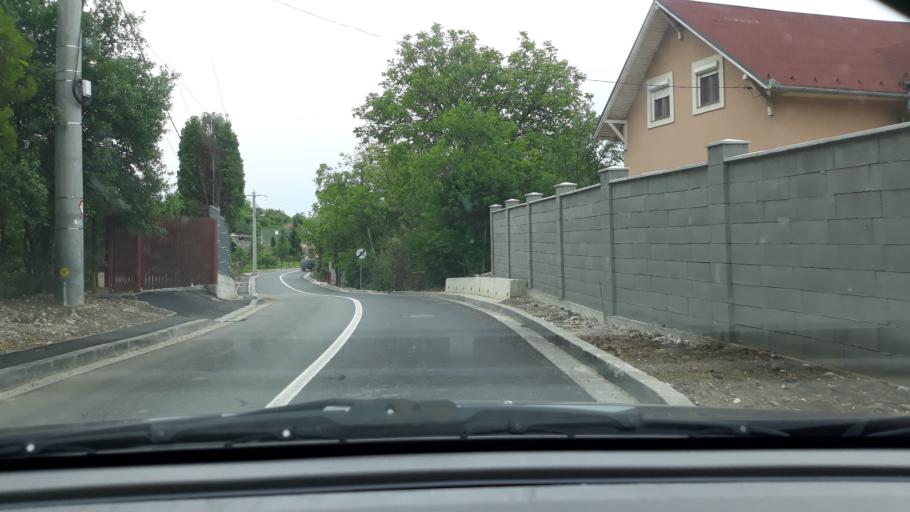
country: RO
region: Bihor
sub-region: Comuna Osorheiu
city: Osorheiu
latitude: 47.0593
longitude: 22.0154
